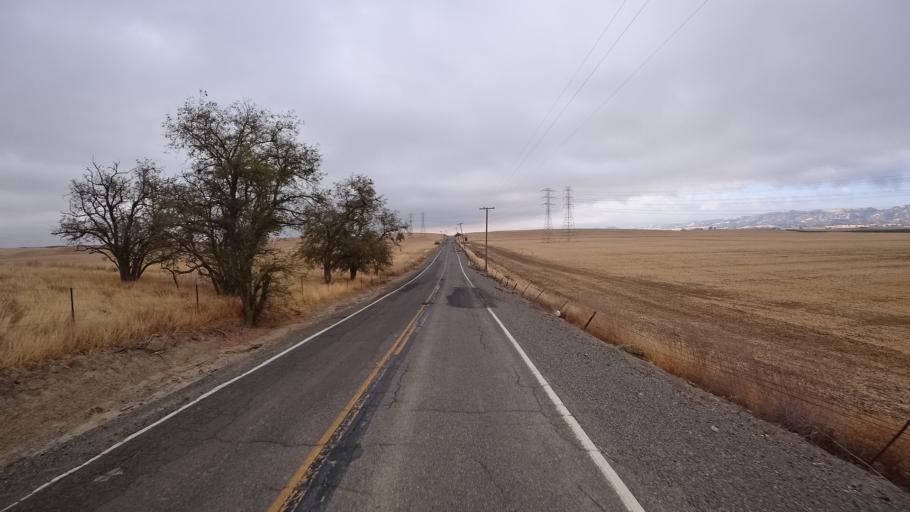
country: US
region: California
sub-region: Yolo County
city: Dunnigan
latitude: 38.8316
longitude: -122.0435
